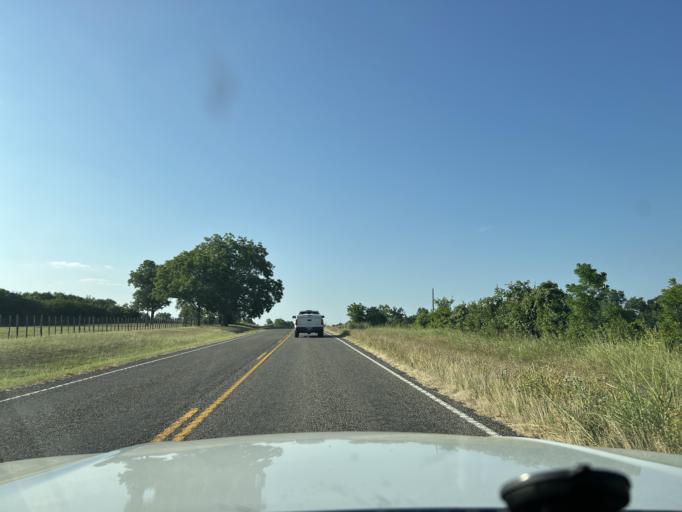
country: US
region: Texas
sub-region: Washington County
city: Brenham
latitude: 30.2296
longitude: -96.2384
